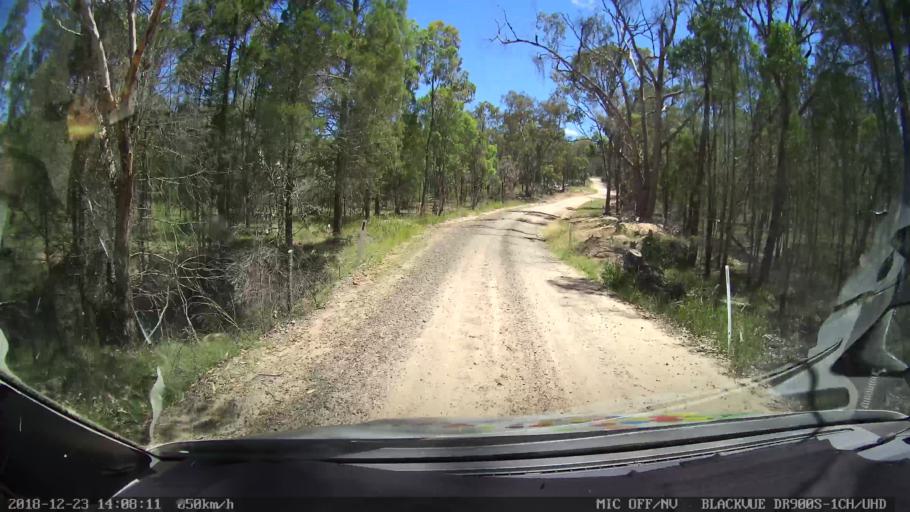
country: AU
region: New South Wales
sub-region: Tamworth Municipality
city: Manilla
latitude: -30.6408
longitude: 151.0694
